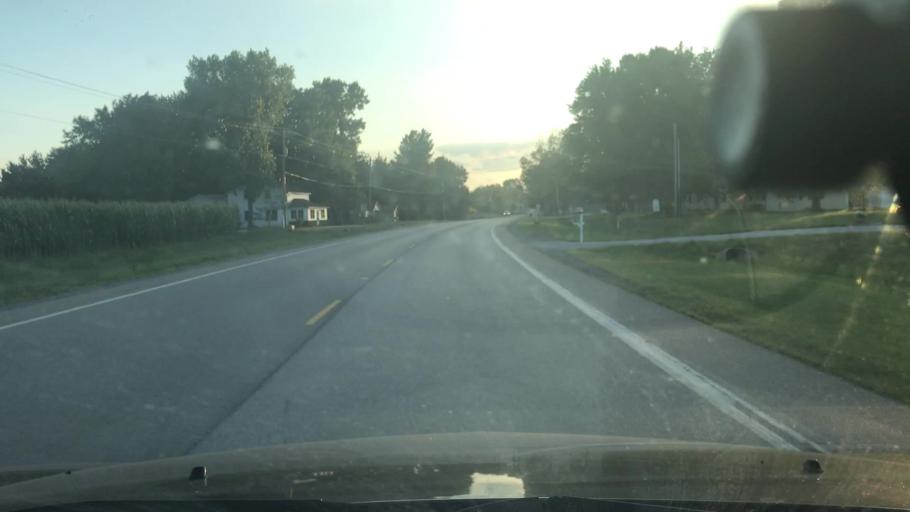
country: US
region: Illinois
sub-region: Washington County
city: Okawville
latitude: 38.4360
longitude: -89.5400
